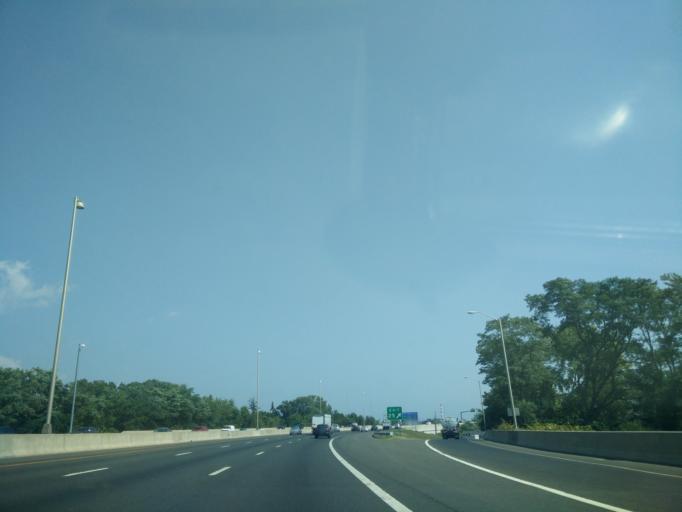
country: US
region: Connecticut
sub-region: Fairfield County
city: Bridgeport
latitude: 41.1678
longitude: -73.2276
